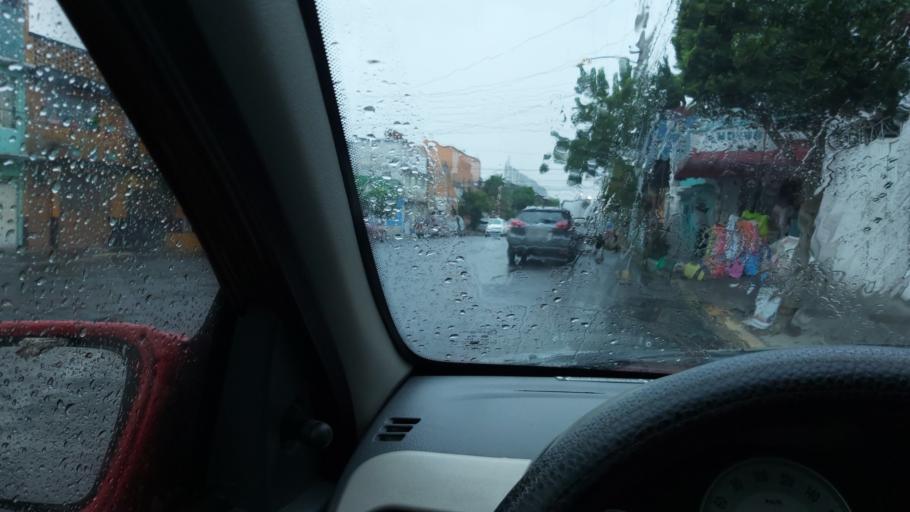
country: MX
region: Mexico
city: Ciudad Nezahualcoyotl
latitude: 19.3905
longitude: -99.0255
